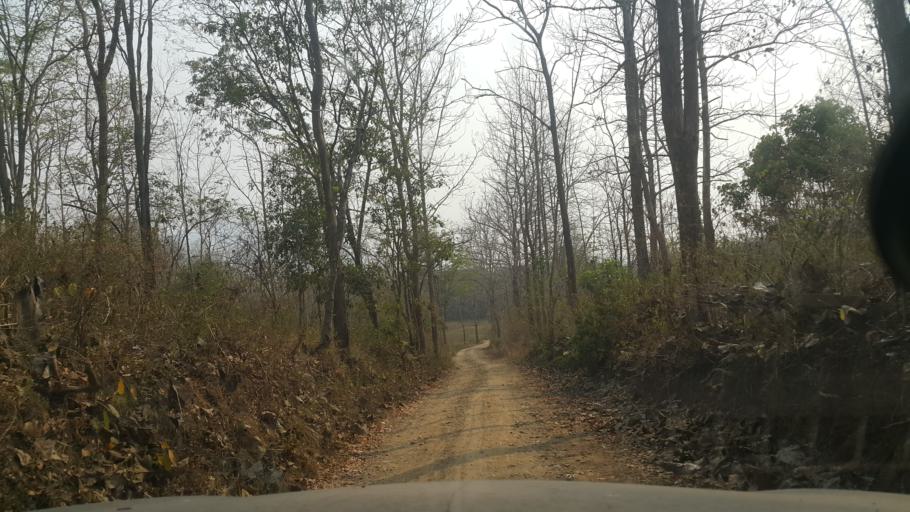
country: TH
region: Chiang Mai
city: Mae On
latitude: 18.7753
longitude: 99.2647
